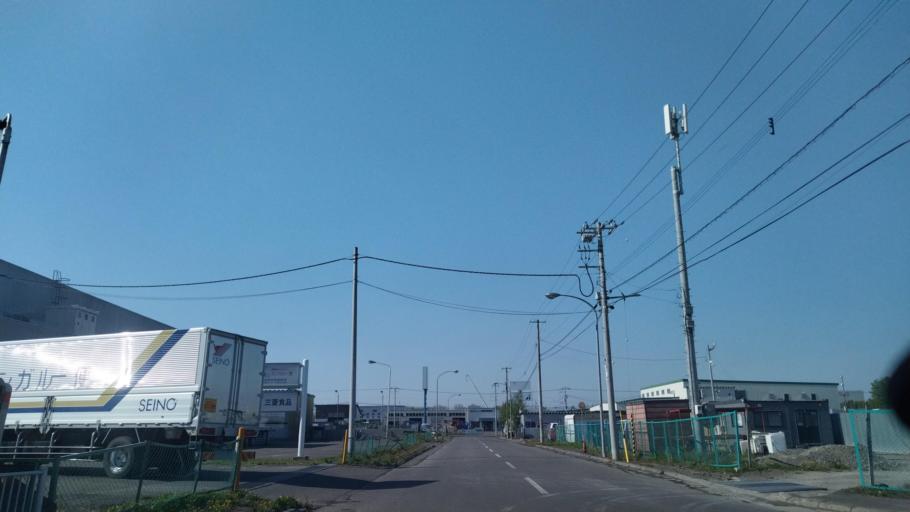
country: JP
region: Hokkaido
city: Obihiro
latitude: 42.9244
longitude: 143.0861
